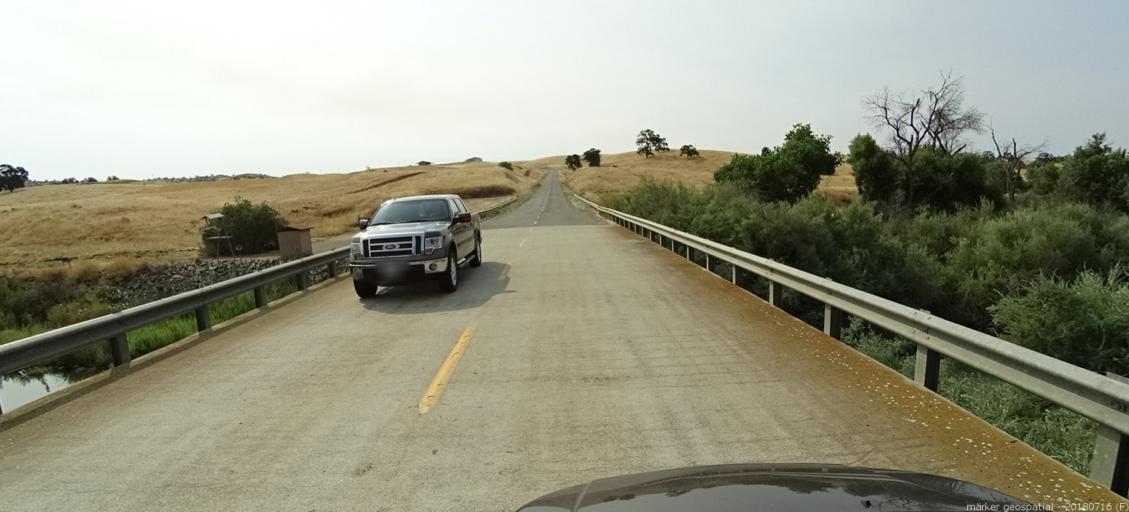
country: US
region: California
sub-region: Madera County
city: Bonadelle Ranchos-Madera Ranchos
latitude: 37.1041
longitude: -119.8883
